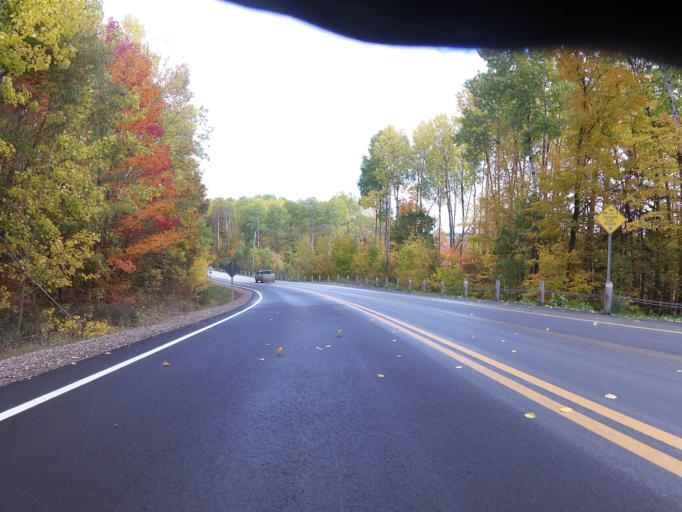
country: CA
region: Ontario
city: Petawawa
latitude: 45.8096
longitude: -77.3474
